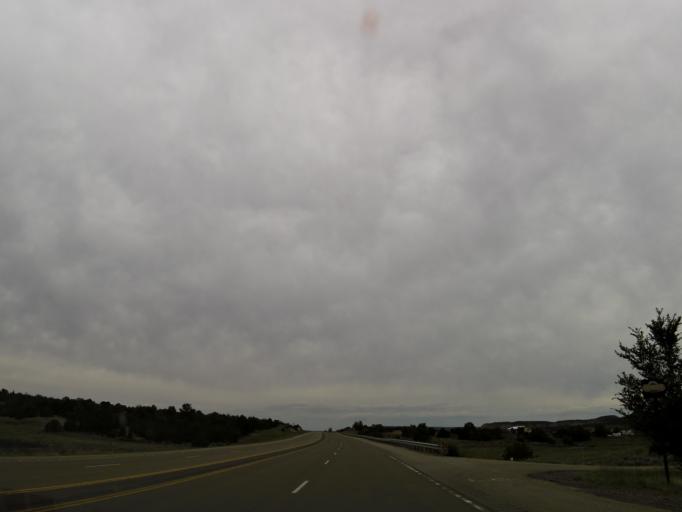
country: US
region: New Mexico
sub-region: Rio Arriba County
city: Santa Teresa
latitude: 36.0035
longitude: -106.9755
